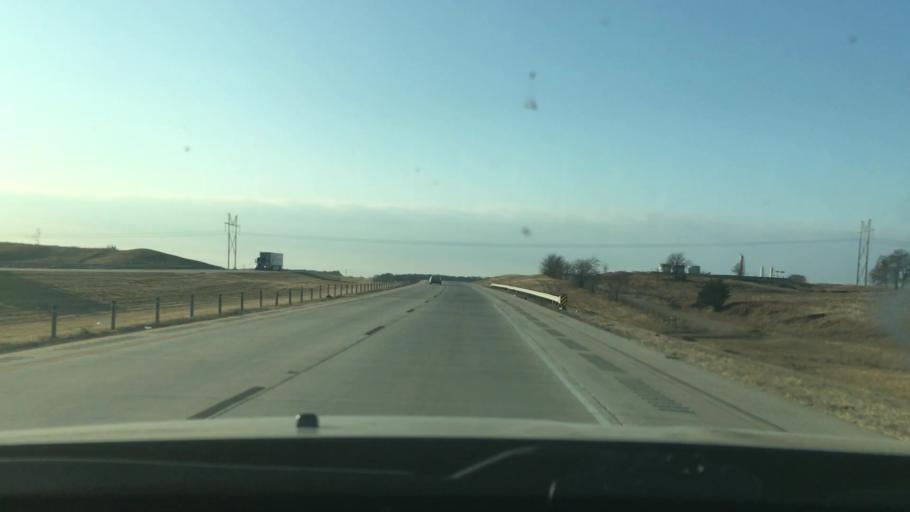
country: US
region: Oklahoma
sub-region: Carter County
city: Ardmore
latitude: 34.2557
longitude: -97.1653
